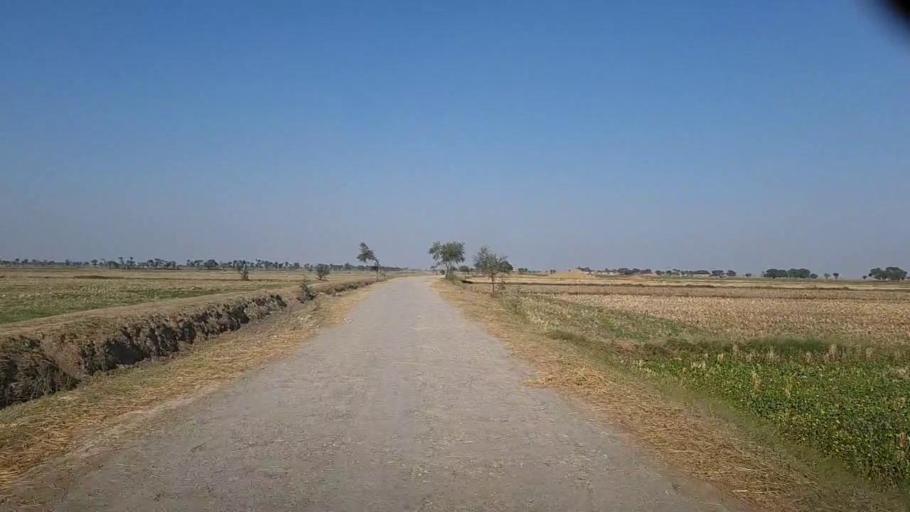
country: PK
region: Sindh
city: Thul
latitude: 28.3481
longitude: 68.7616
